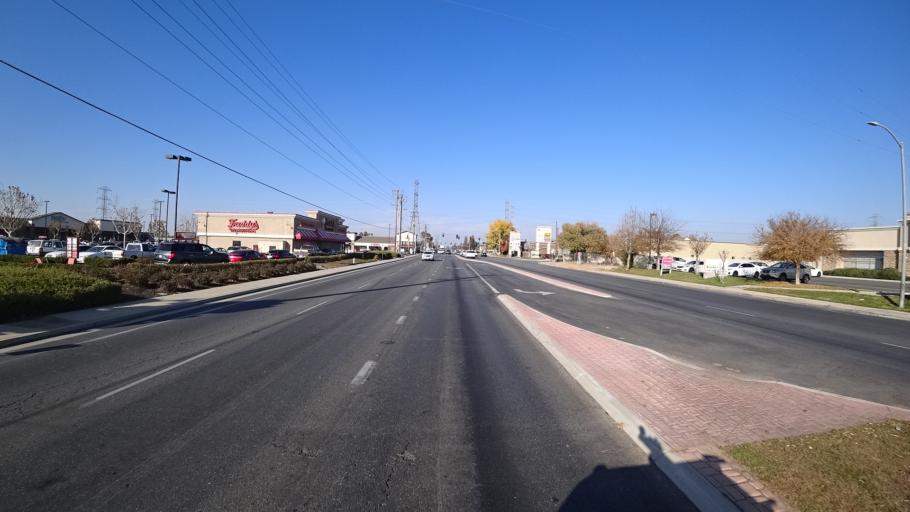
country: US
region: California
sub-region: Kern County
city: Greenacres
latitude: 35.3849
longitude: -119.1100
